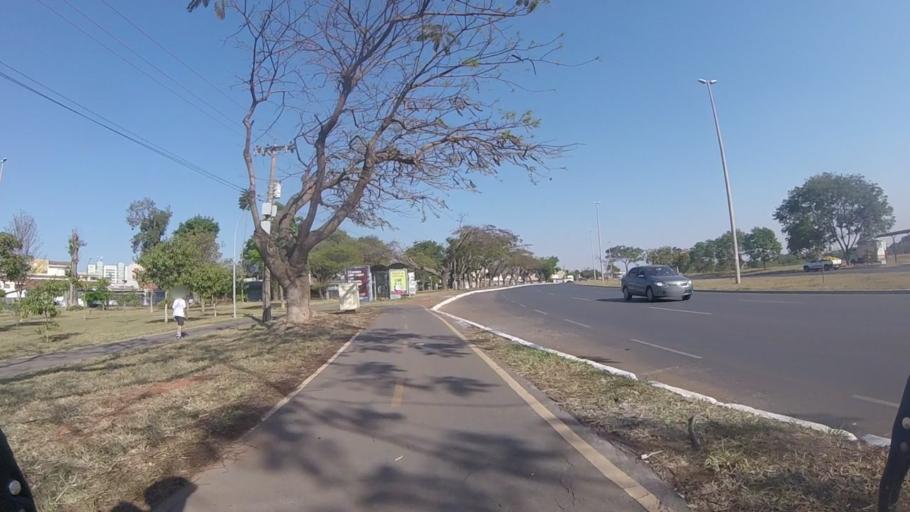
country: BR
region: Federal District
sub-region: Brasilia
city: Brasilia
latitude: -15.8356
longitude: -47.9743
